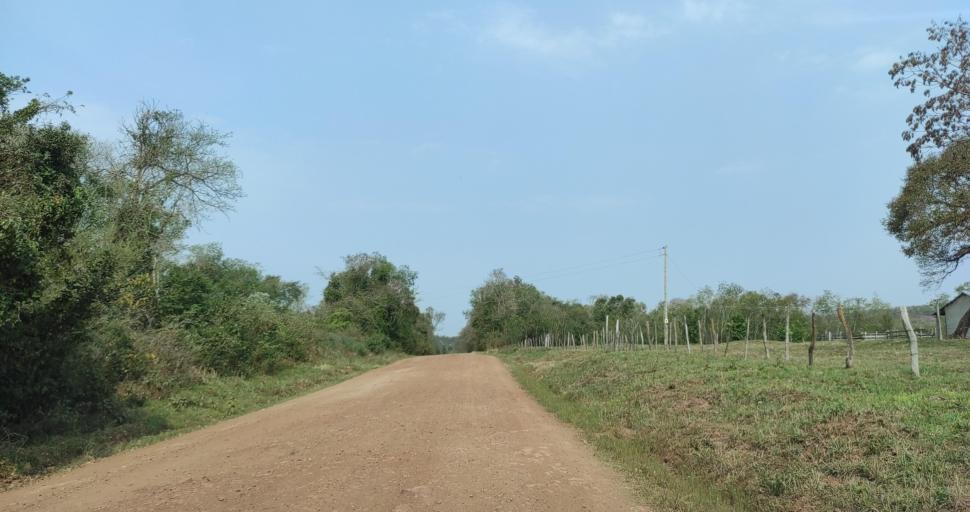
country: AR
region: Misiones
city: Cerro Cora
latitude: -27.5214
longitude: -55.5999
